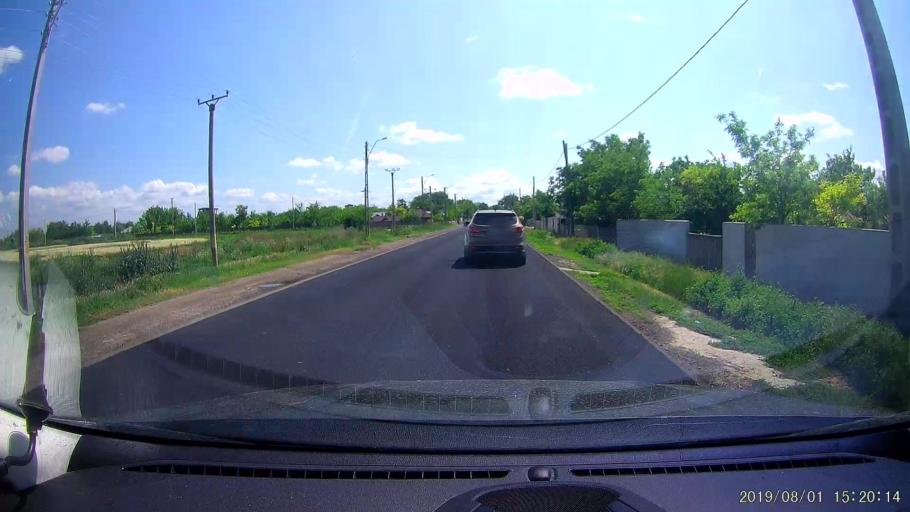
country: RO
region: Braila
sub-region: Comuna Tufesti
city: Tufesti
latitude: 45.0810
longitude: 27.8081
